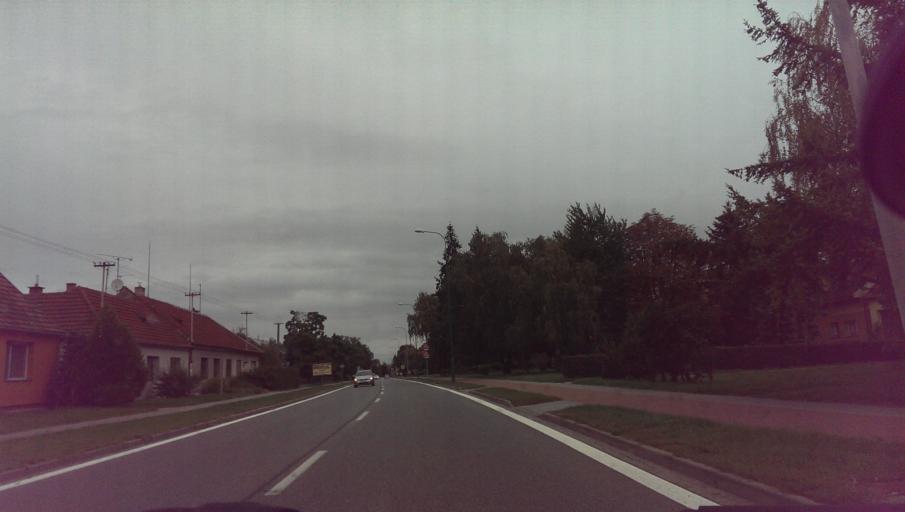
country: CZ
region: South Moravian
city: Bzenec
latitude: 48.9708
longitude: 17.2747
